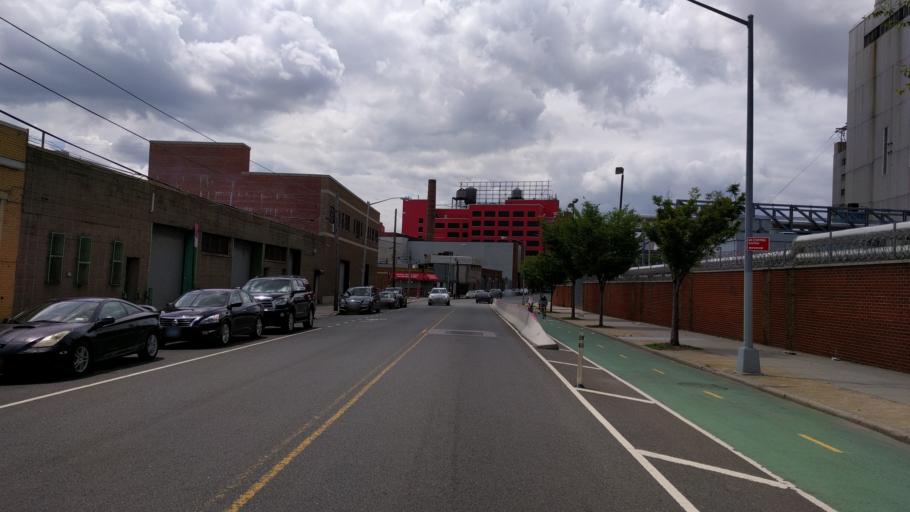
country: US
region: New York
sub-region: Queens County
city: Long Island City
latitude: 40.7601
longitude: -73.9437
